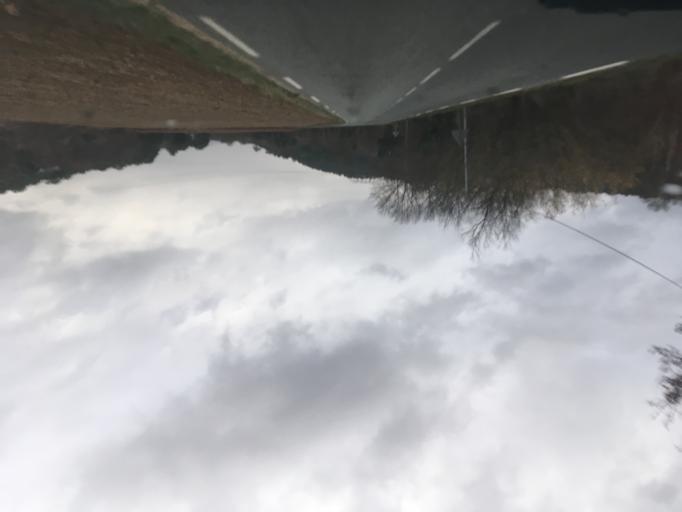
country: FR
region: Provence-Alpes-Cote d'Azur
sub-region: Departement du Var
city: Sainte-Anastasie-sur-Issole
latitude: 43.3394
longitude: 6.1447
